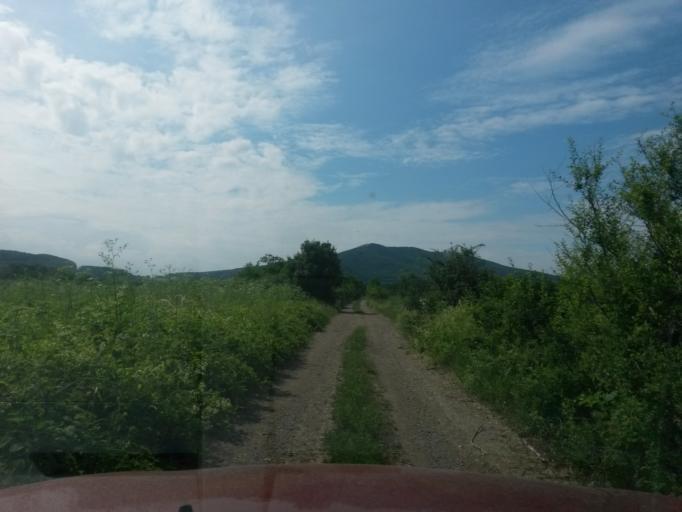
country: SK
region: Kosicky
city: Secovce
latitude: 48.6256
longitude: 21.5025
